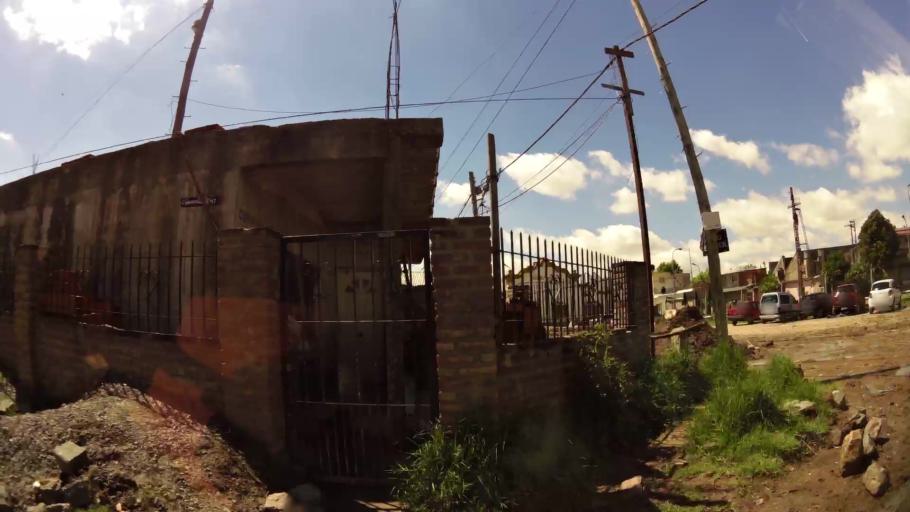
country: AR
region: Buenos Aires
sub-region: Partido de Lanus
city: Lanus
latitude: -34.6608
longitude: -58.4163
